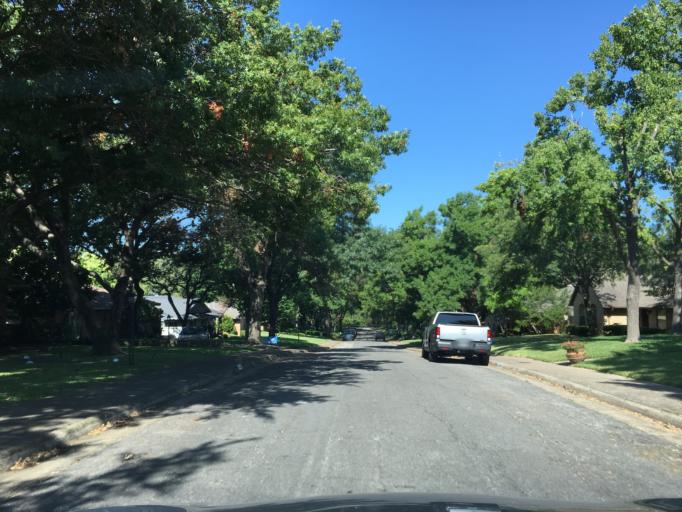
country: US
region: Texas
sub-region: Dallas County
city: Garland
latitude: 32.8585
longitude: -96.6935
